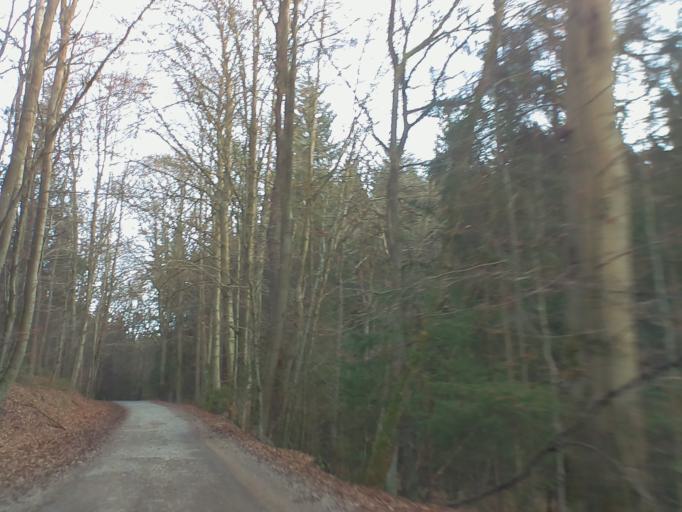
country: DE
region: Thuringia
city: Hummelshain
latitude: 50.7536
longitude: 11.6459
